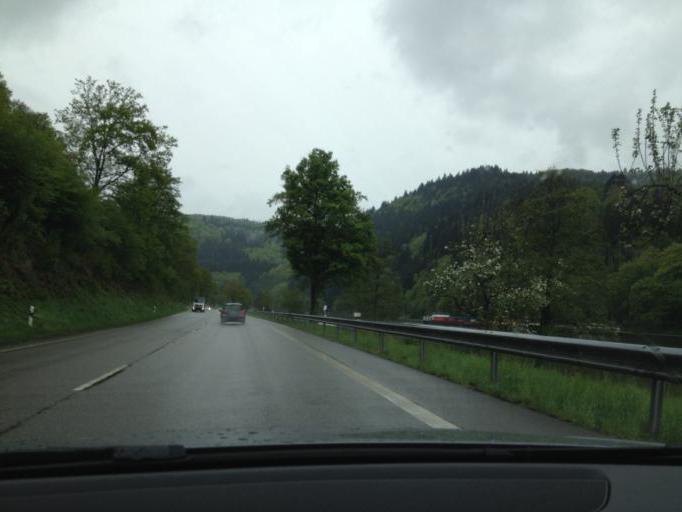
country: DE
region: Baden-Wuerttemberg
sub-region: Karlsruhe Region
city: Zwingenberg
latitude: 49.4292
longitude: 9.0051
